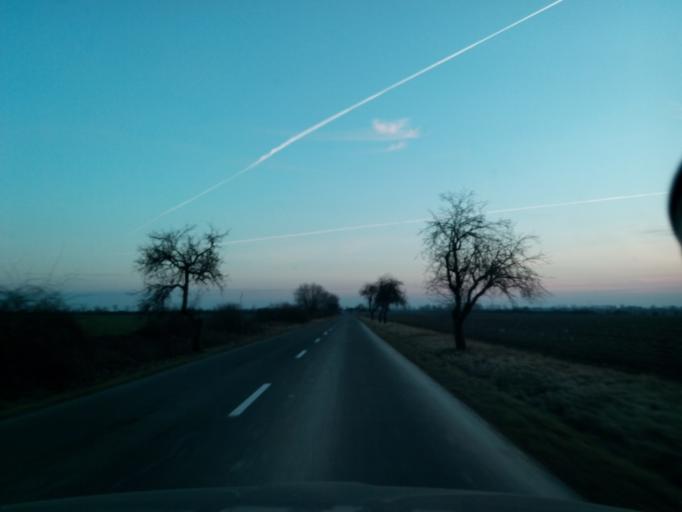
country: SK
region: Kosicky
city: Sobrance
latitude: 48.7764
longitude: 22.1282
